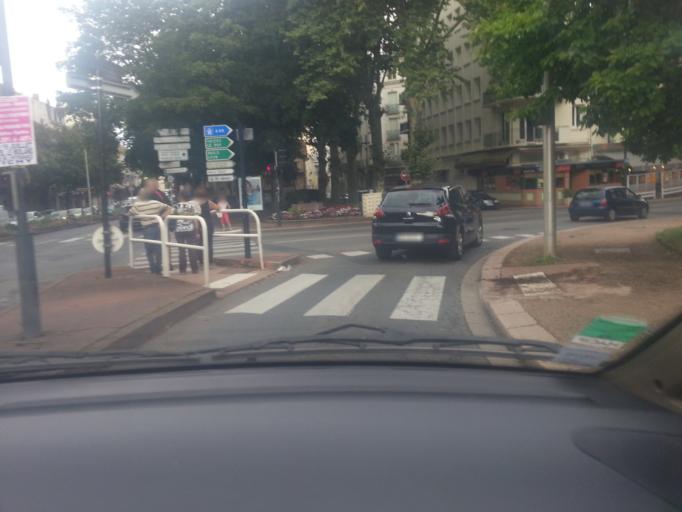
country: FR
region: Auvergne
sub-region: Departement de l'Allier
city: Vichy
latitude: 46.1205
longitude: 3.4190
